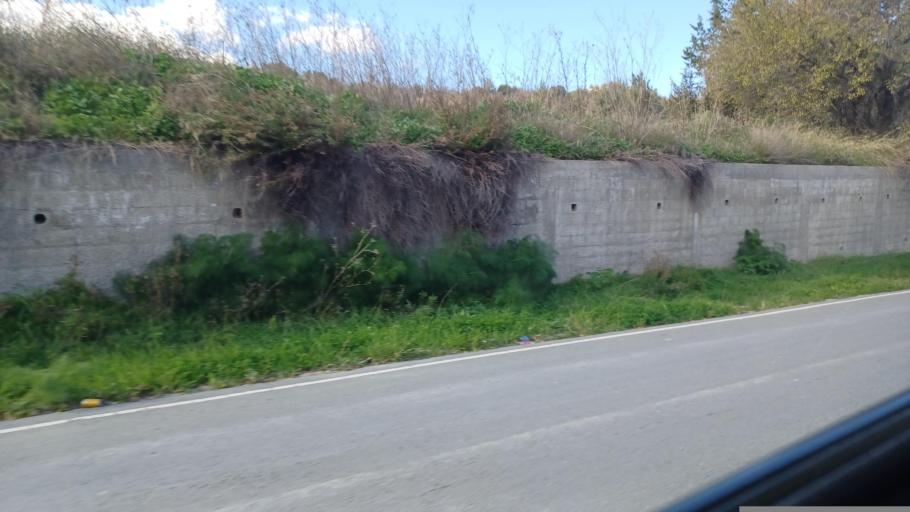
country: CY
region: Limassol
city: Pelendri
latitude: 34.8100
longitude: 32.9608
